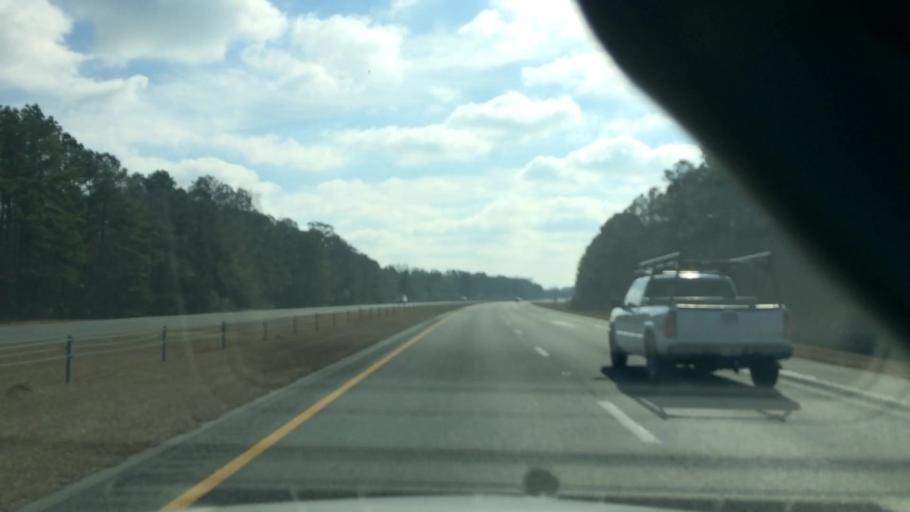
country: US
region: North Carolina
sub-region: Duplin County
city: Wallace
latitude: 34.6992
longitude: -77.9449
